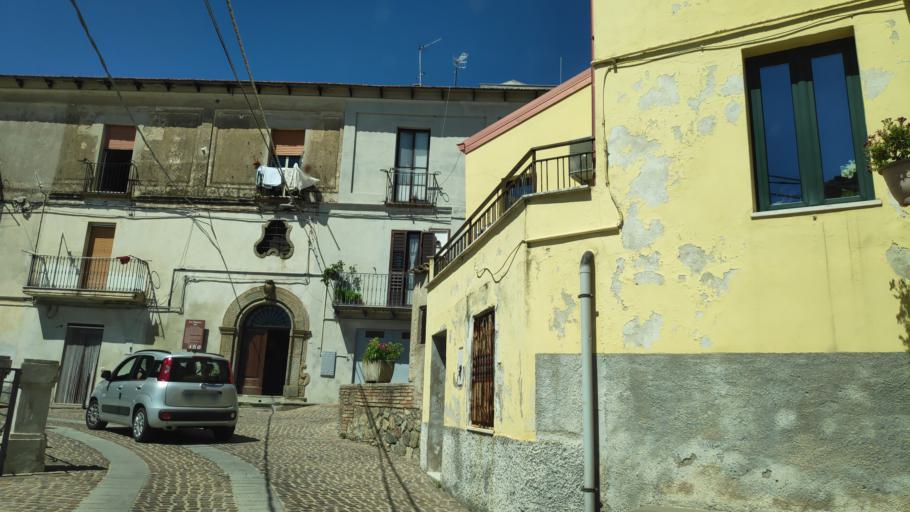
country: IT
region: Calabria
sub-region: Provincia di Catanzaro
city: Montauro
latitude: 38.7477
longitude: 16.5113
